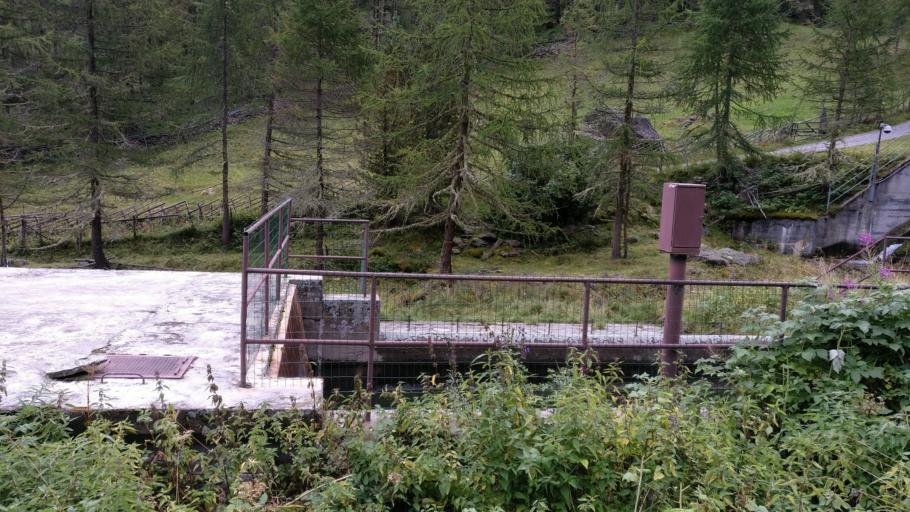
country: IT
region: Trentino-Alto Adige
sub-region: Bolzano
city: Senales
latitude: 46.6973
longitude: 10.8847
